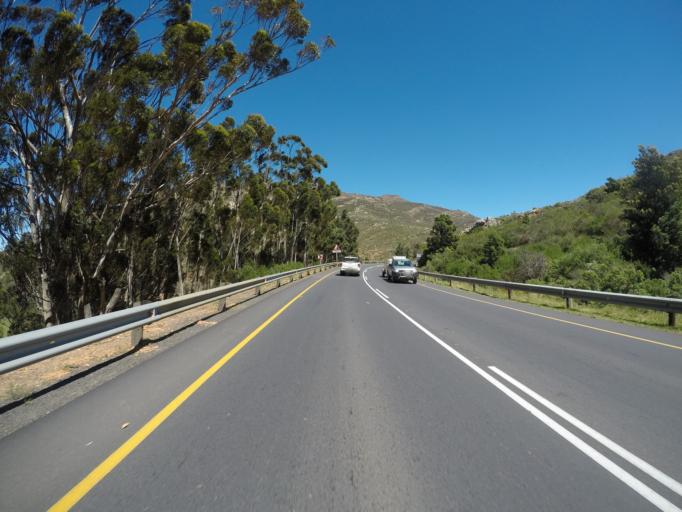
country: ZA
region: Western Cape
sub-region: Cape Winelands District Municipality
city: Ceres
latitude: -33.3171
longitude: 19.0916
